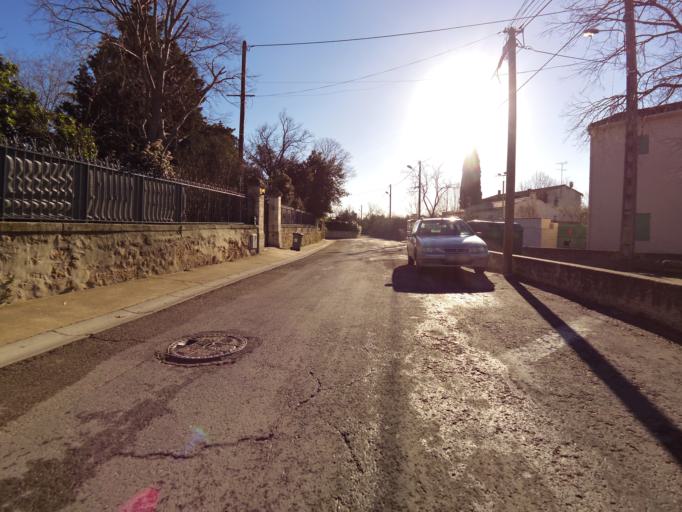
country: FR
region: Languedoc-Roussillon
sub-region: Departement du Gard
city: Aigues-Vives
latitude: 43.7419
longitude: 4.1690
